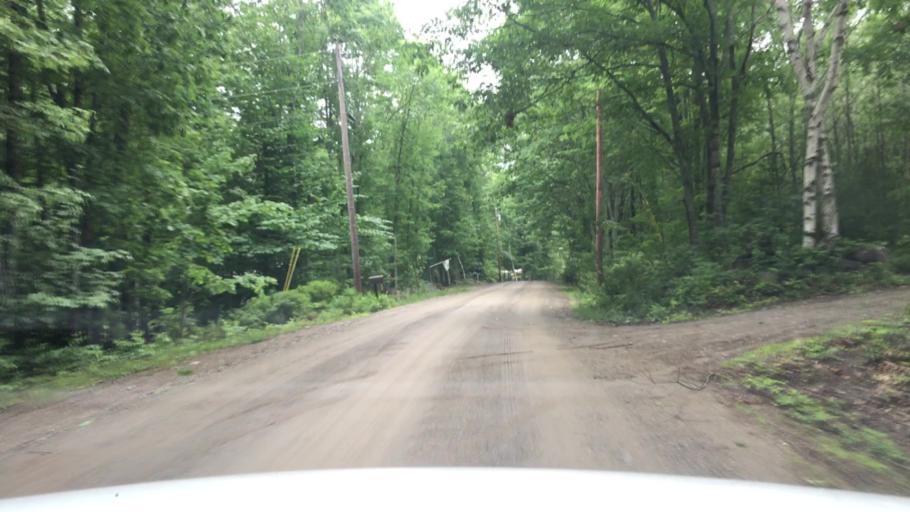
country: US
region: Maine
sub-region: Knox County
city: Hope
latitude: 44.2402
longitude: -69.1819
